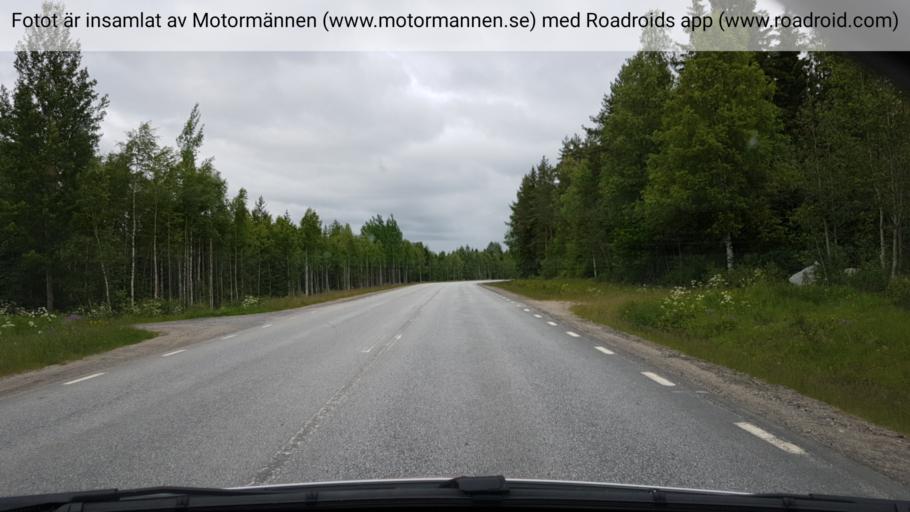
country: SE
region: Vaesterbotten
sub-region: Vannas Kommun
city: Vaennaes
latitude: 63.9317
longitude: 19.7727
